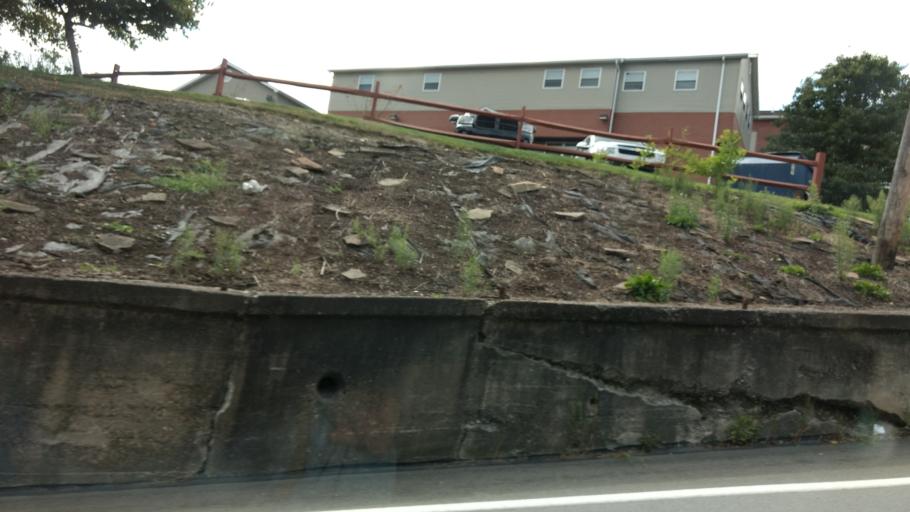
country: US
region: Pennsylvania
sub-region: Washington County
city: North Charleroi
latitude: 40.1530
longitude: -79.9082
